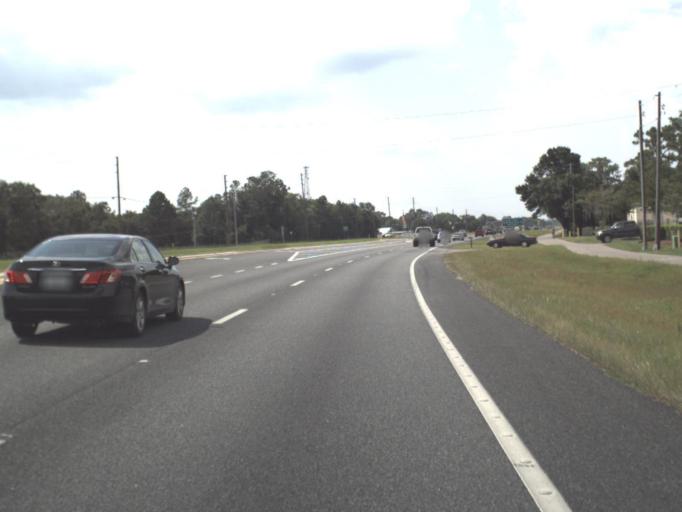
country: US
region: Florida
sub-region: Pasco County
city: Land O' Lakes
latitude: 28.2558
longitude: -82.4722
